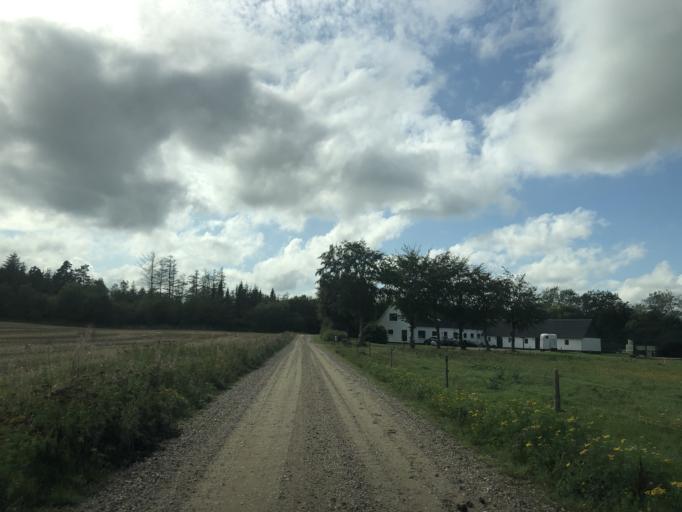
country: DK
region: Central Jutland
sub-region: Holstebro Kommune
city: Ulfborg
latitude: 56.2335
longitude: 8.4411
